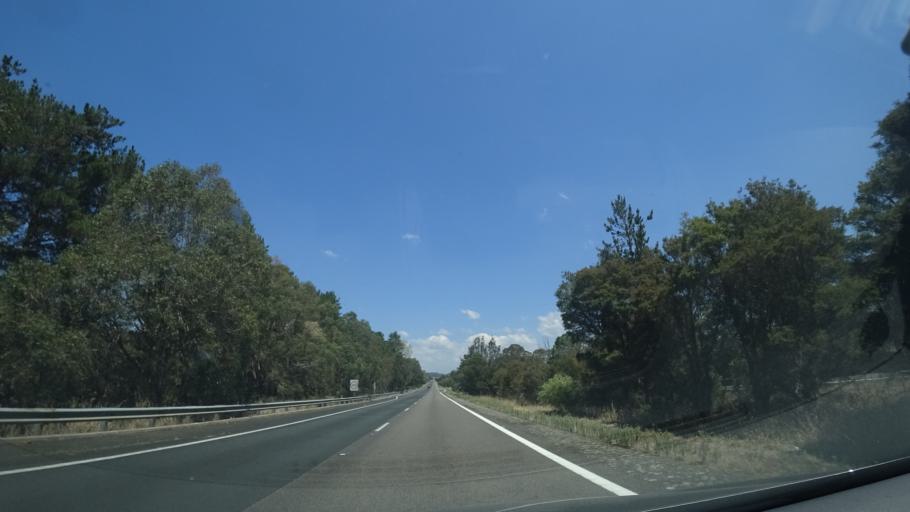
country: AU
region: New South Wales
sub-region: Wingecarribee
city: Bundanoon
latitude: -34.5671
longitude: 150.2545
